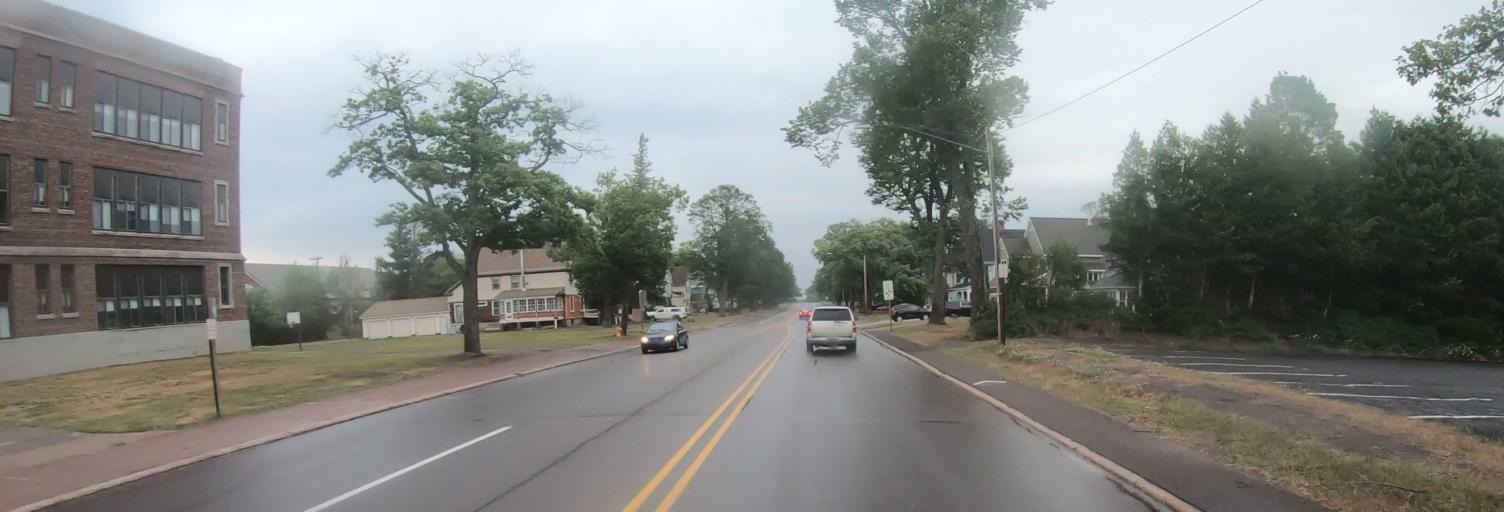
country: US
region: Michigan
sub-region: Houghton County
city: Laurium
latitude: 47.2418
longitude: -88.4458
